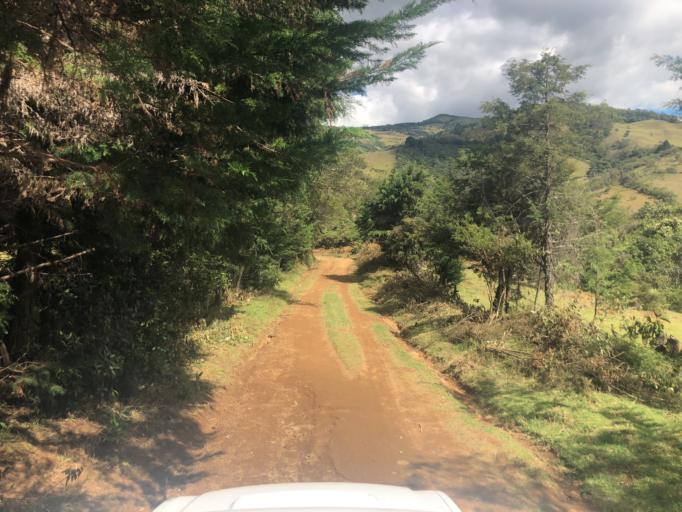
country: CO
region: Cauca
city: Silvia
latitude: 2.6846
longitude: -76.4378
